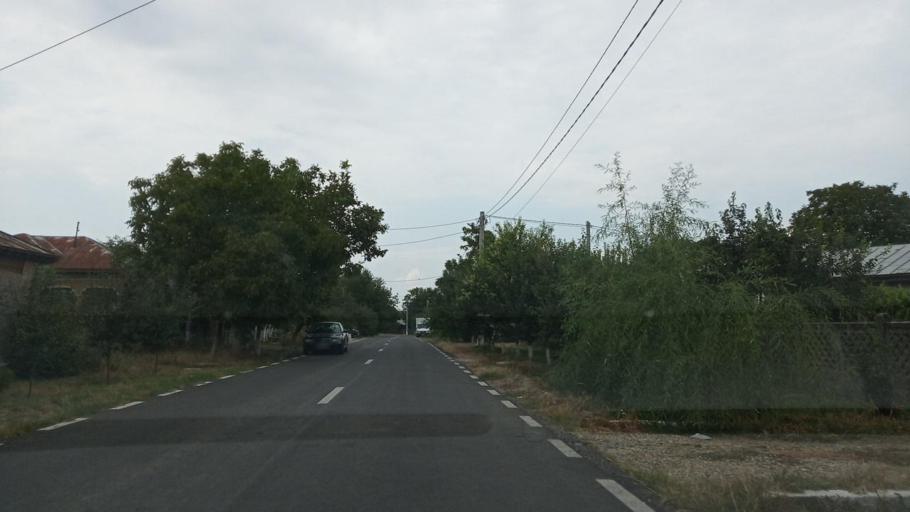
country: RO
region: Giurgiu
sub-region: Comuna Gostinari
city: Gostinari
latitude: 44.1705
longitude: 26.2489
